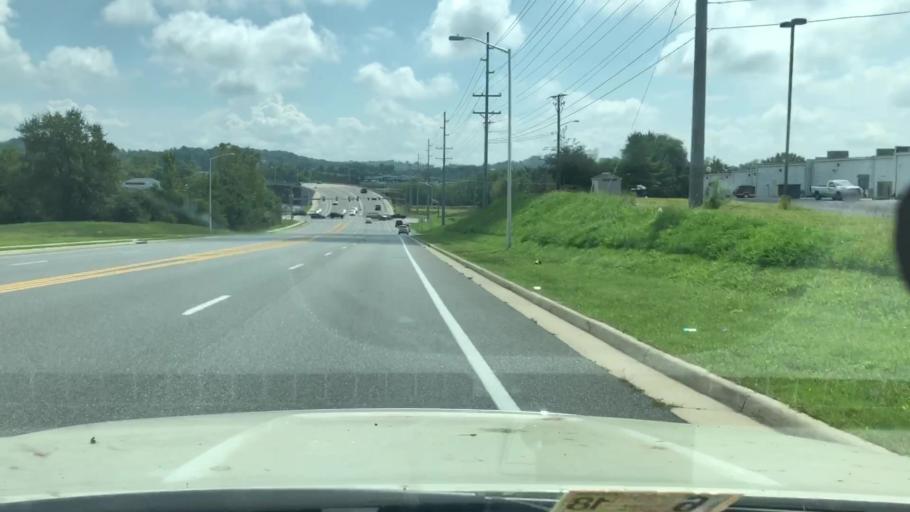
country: US
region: Virginia
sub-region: City of Harrisonburg
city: Harrisonburg
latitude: 38.4238
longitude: -78.8941
